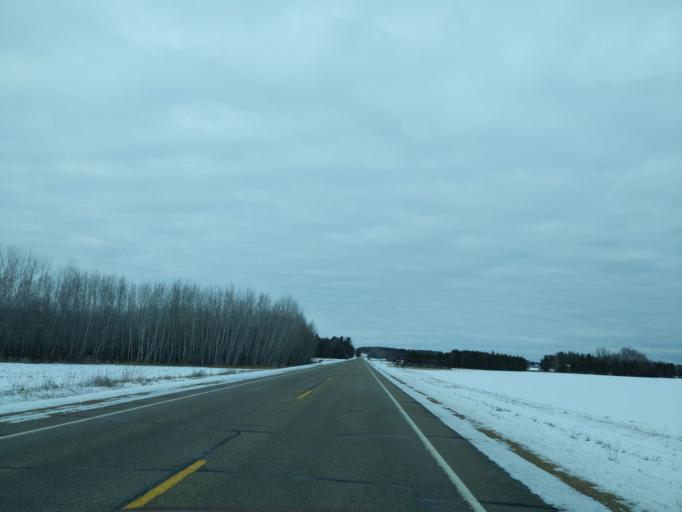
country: US
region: Wisconsin
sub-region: Waushara County
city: Wautoma
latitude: 43.9905
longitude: -89.3276
